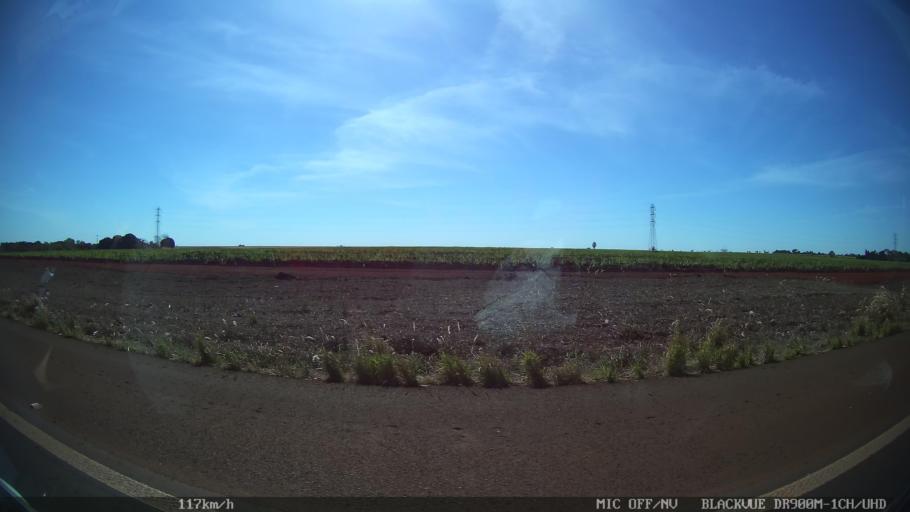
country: BR
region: Sao Paulo
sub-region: Guaira
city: Guaira
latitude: -20.4456
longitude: -48.4051
